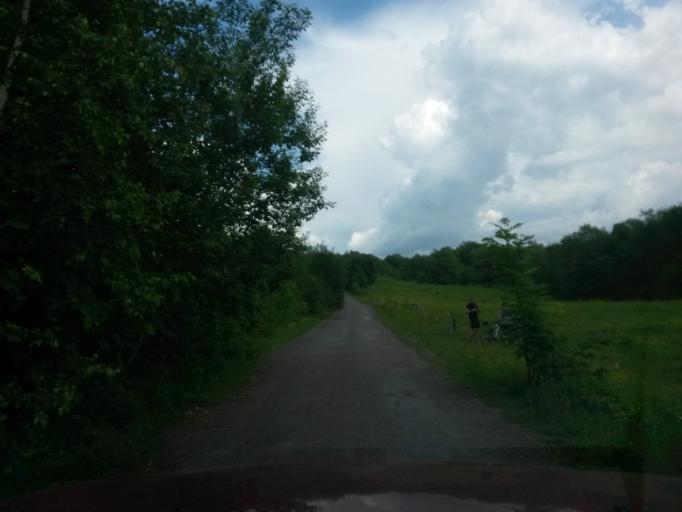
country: UA
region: Zakarpattia
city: Velykyi Bereznyi
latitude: 48.8999
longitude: 22.5047
